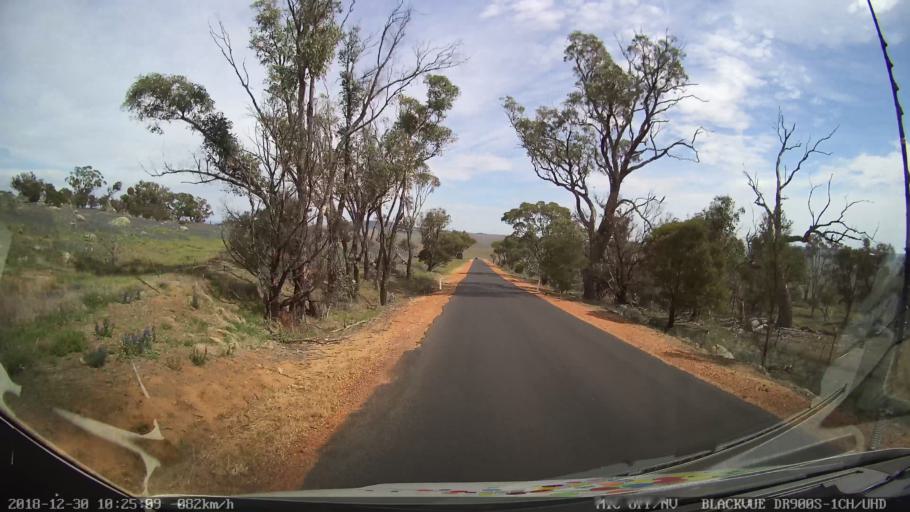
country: AU
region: New South Wales
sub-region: Snowy River
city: Berridale
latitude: -36.5281
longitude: 148.9612
